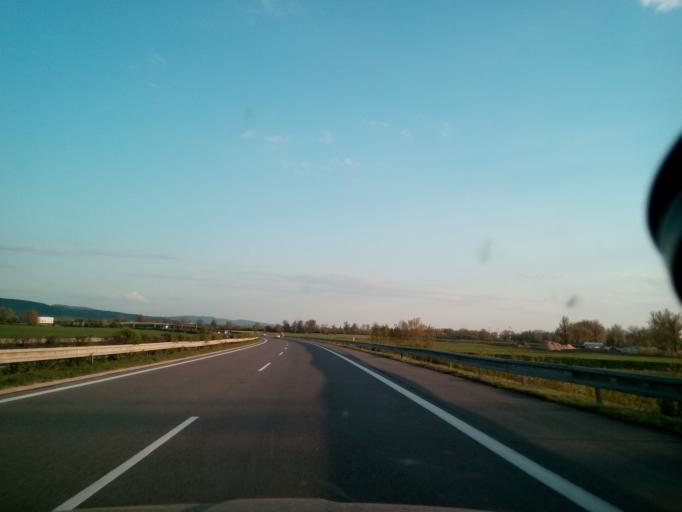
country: SK
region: Trenciansky
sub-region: Okres Nove Mesto nad Vahom
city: Nove Mesto nad Vahom
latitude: 48.7464
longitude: 17.8599
